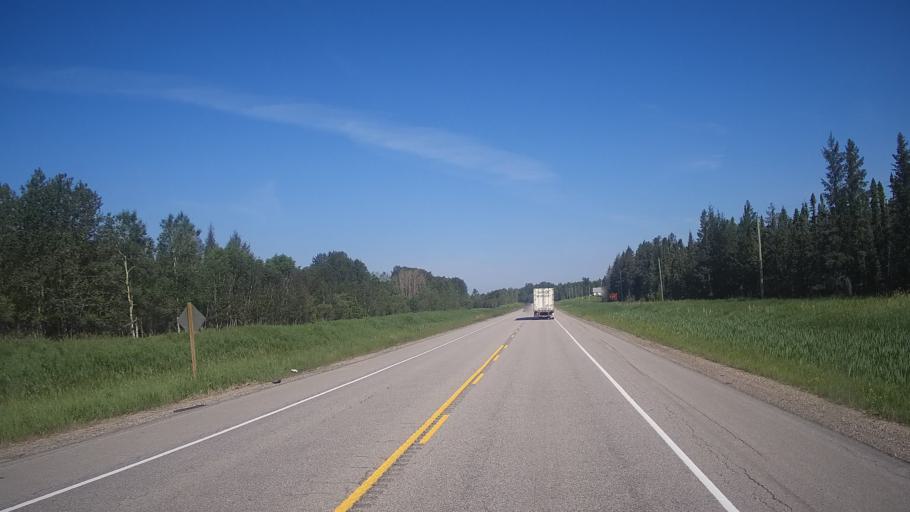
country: CA
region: Ontario
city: Dryden
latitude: 49.6991
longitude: -92.5702
